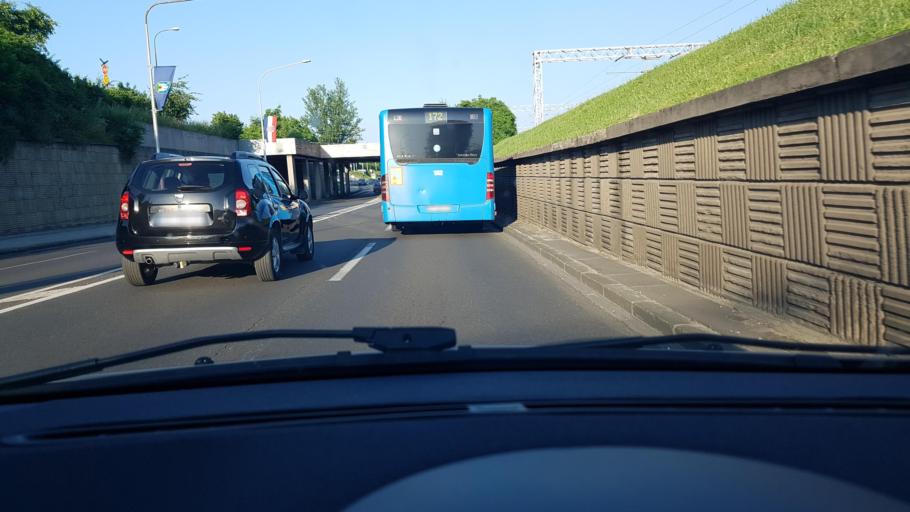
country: HR
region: Grad Zagreb
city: Stenjevec
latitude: 45.8145
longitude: 15.8591
